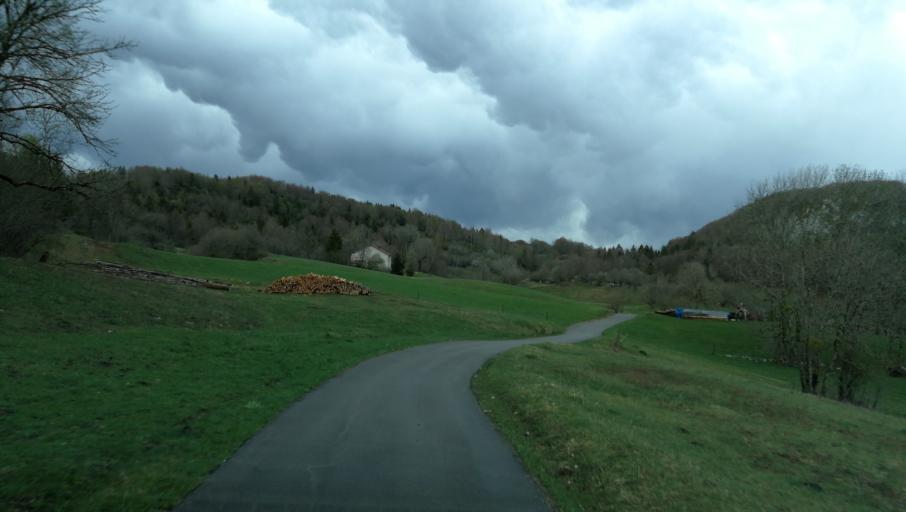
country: FR
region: Franche-Comte
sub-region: Departement du Jura
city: Lavans-les-Saint-Claude
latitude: 46.3166
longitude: 5.8072
